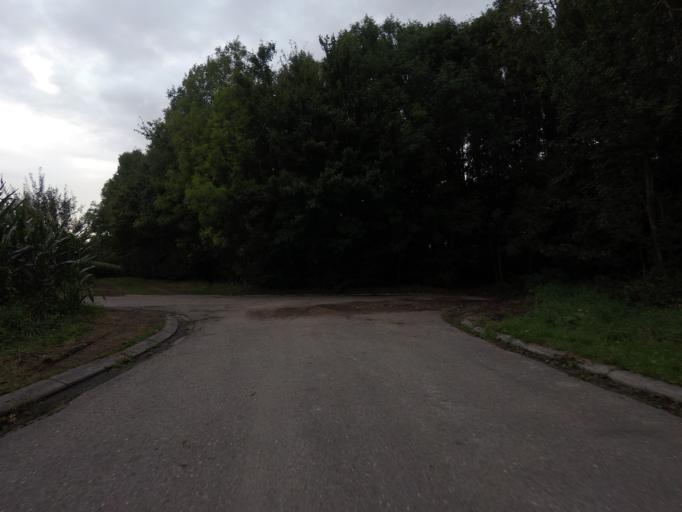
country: BE
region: Flanders
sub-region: Provincie Antwerpen
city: Willebroek
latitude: 51.0353
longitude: 4.3484
